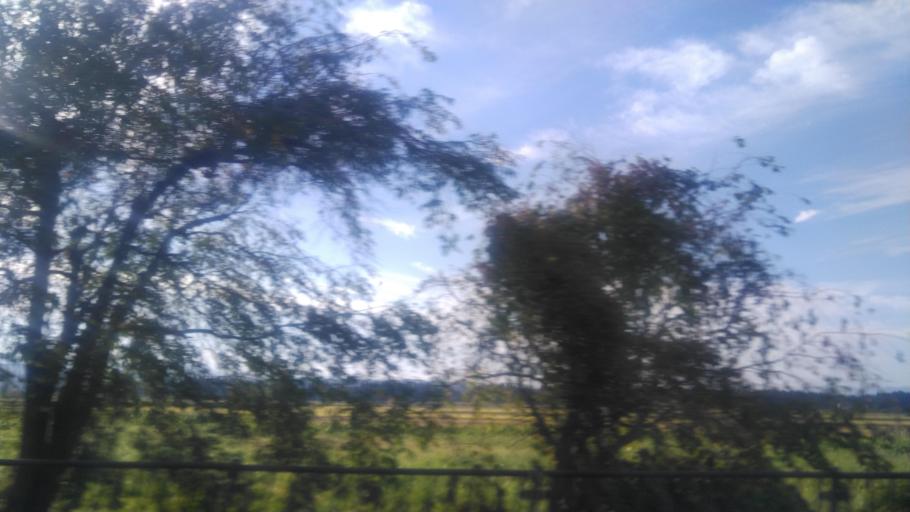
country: JP
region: Akita
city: Takanosu
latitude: 40.2526
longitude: 140.3834
